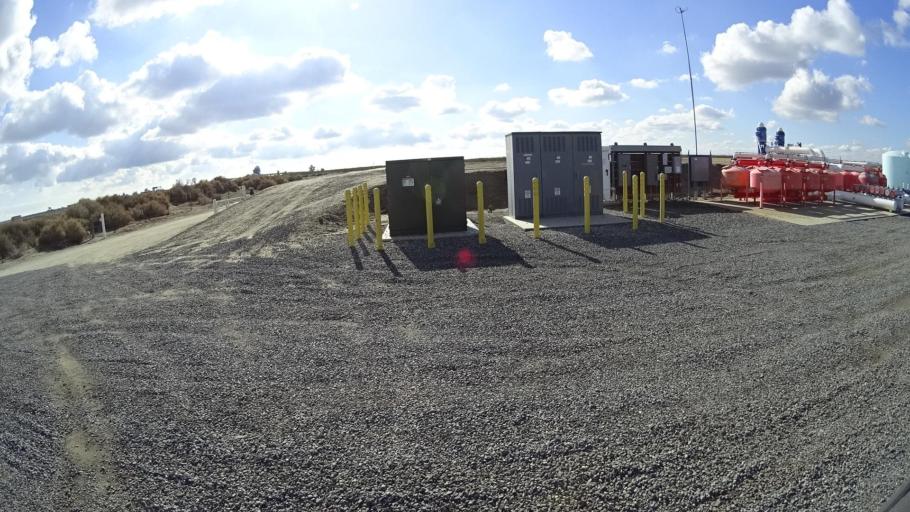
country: US
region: California
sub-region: Kern County
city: McFarland
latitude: 35.6527
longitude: -119.2234
